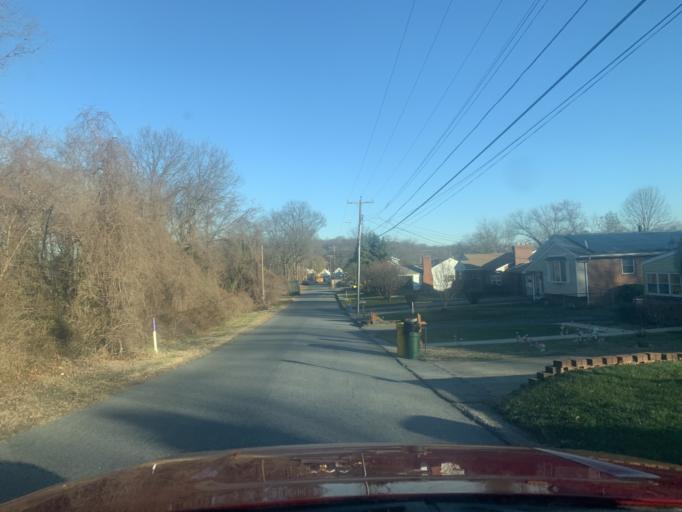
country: US
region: Maryland
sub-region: Anne Arundel County
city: Brooklyn Park
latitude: 39.2041
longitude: -76.6078
